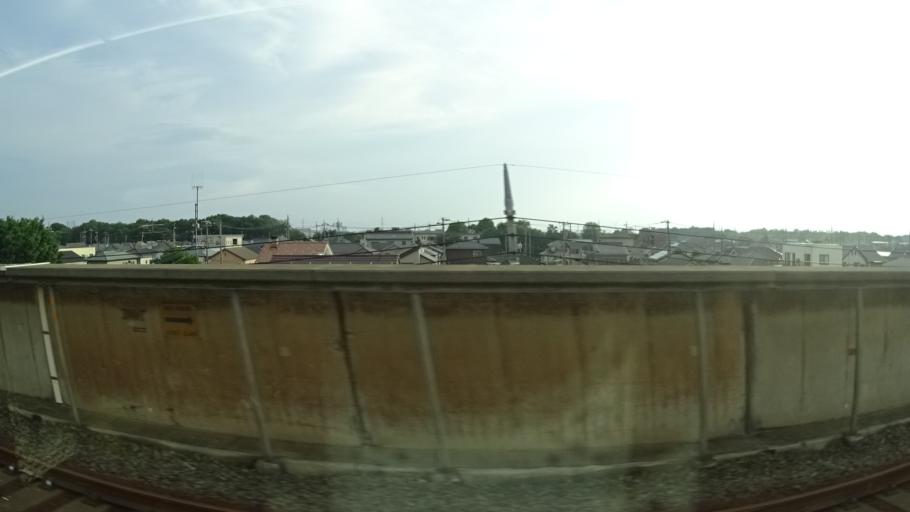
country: JP
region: Saitama
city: Ageoshimo
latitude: 35.9990
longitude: 139.6177
